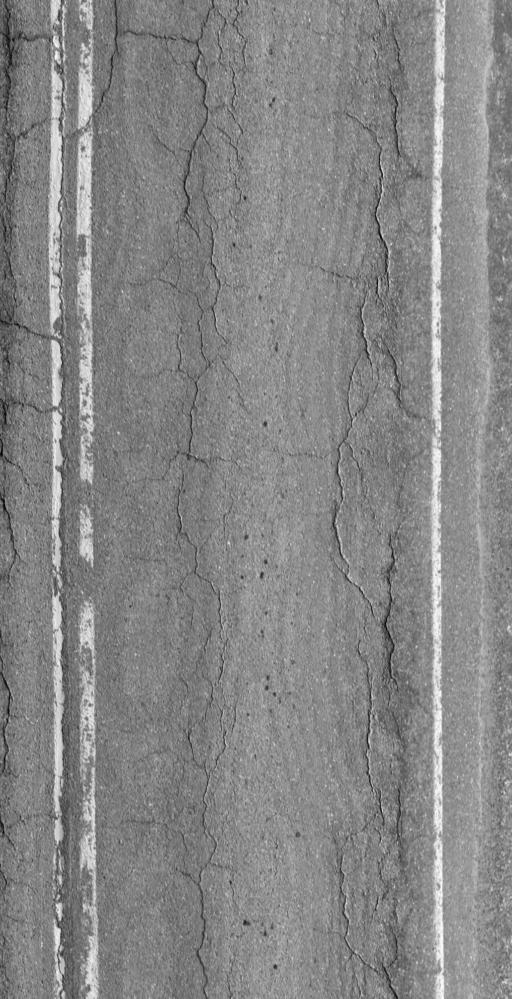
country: US
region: Vermont
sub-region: Chittenden County
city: Jericho
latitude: 44.4574
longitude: -73.0078
